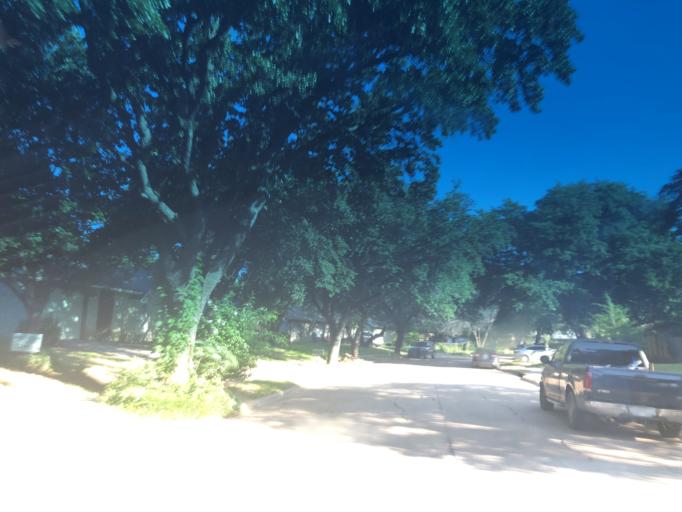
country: US
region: Texas
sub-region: Dallas County
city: Grand Prairie
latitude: 32.6959
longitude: -97.0003
